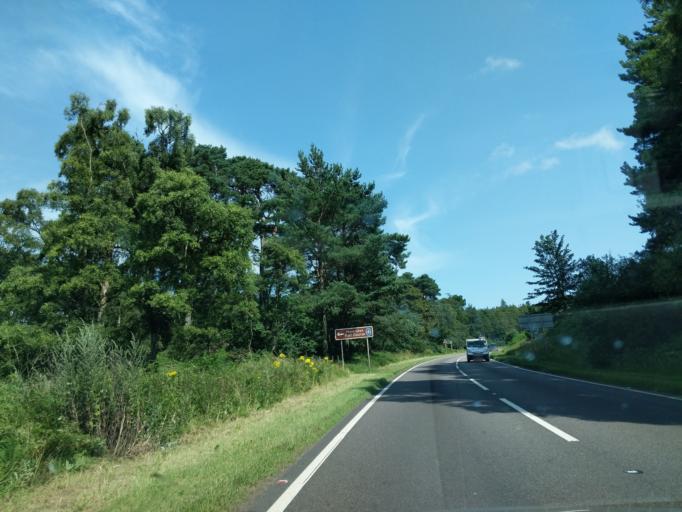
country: GB
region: Scotland
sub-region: Moray
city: Lhanbryd
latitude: 57.6342
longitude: -3.1925
